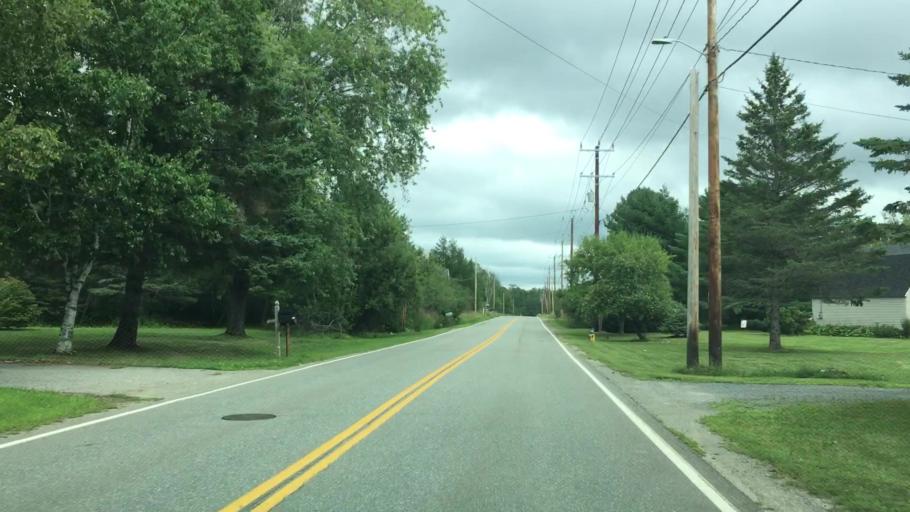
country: US
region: Maine
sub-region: Penobscot County
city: Brewer
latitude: 44.7674
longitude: -68.7645
